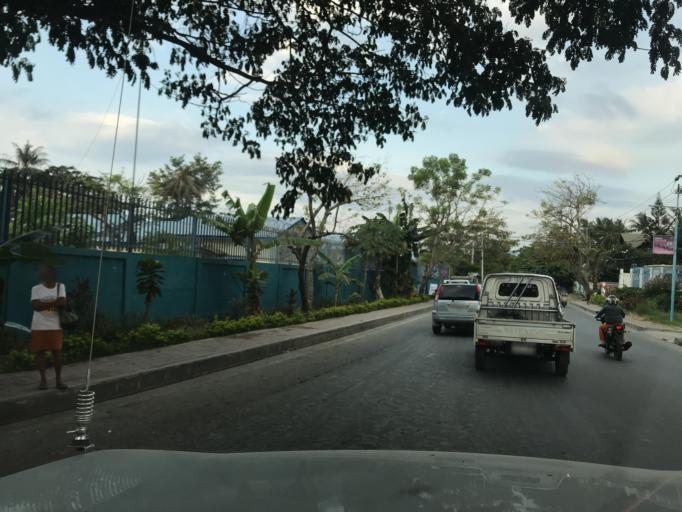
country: TL
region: Dili
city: Dili
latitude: -8.5455
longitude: 125.5459
